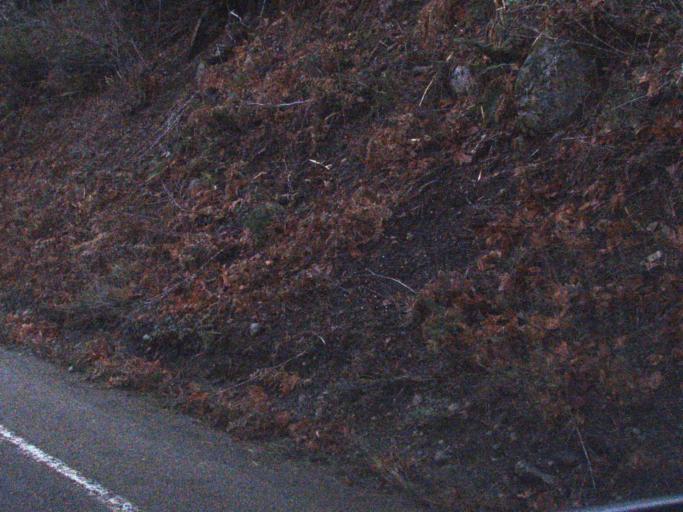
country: US
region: Washington
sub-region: Snohomish County
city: Darrington
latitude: 48.6530
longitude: -121.2989
